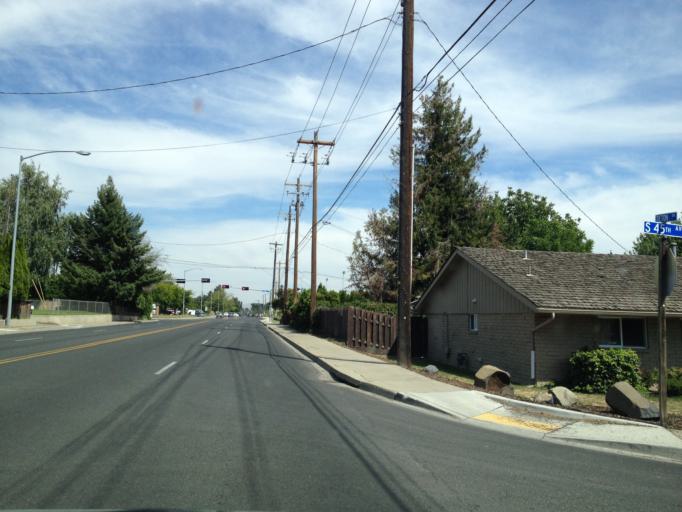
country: US
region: Washington
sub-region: Yakima County
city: West Valley
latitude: 46.5926
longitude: -120.5686
